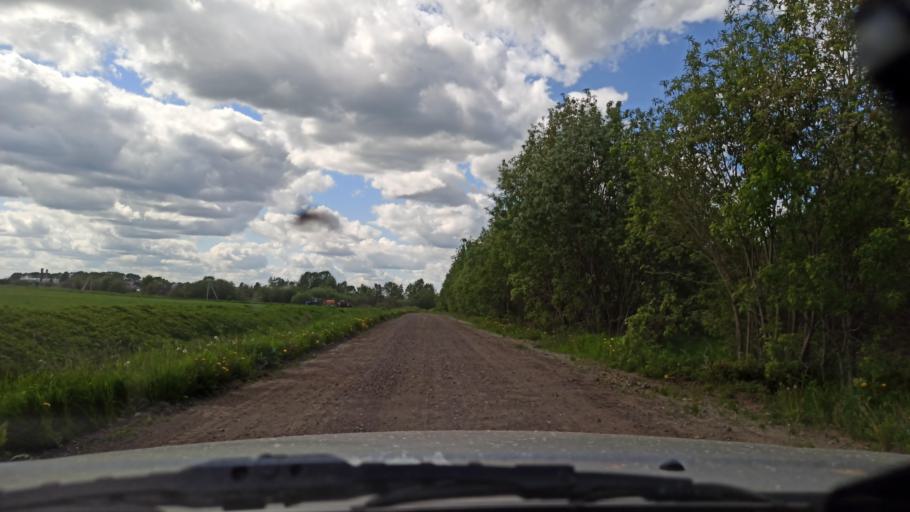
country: RU
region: Vologda
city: Vologda
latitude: 59.3417
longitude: 39.8356
